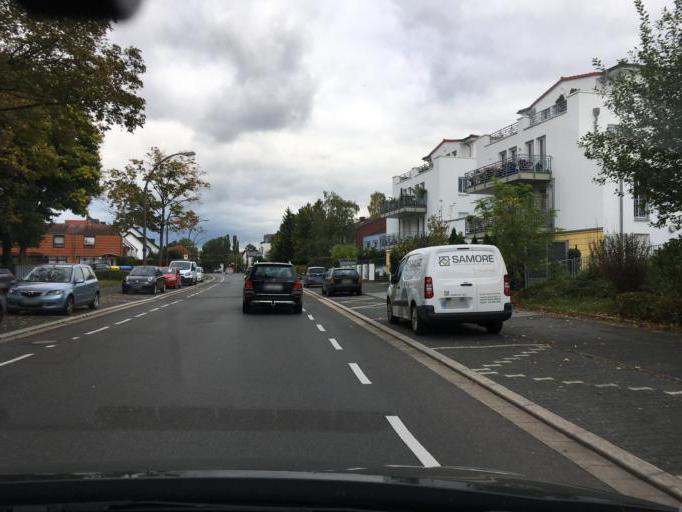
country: DE
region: North Rhine-Westphalia
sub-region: Regierungsbezirk Koln
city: Konigswinter
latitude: 50.6613
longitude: 7.1815
